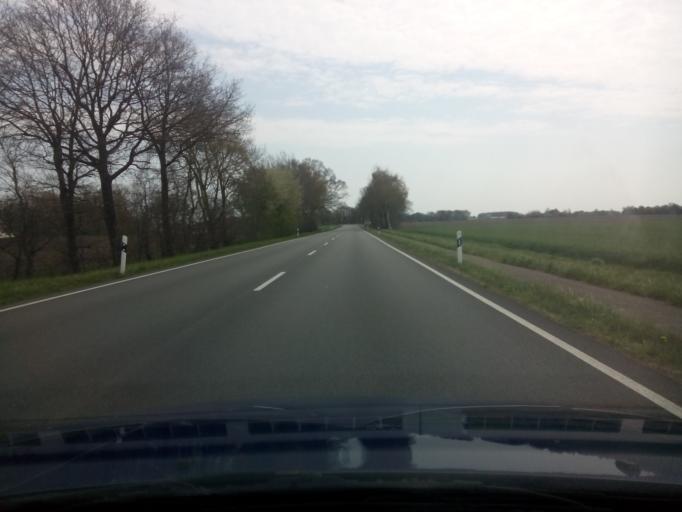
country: DE
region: Lower Saxony
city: Sustedt
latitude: 52.8421
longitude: 8.9022
